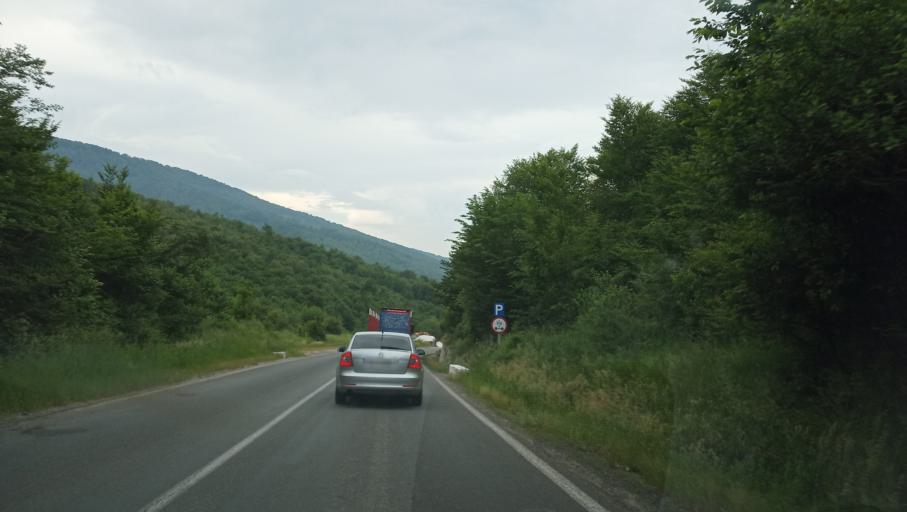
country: RO
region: Caras-Severin
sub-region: Comuna Bautar
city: Bucova
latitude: 45.5069
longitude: 22.6704
